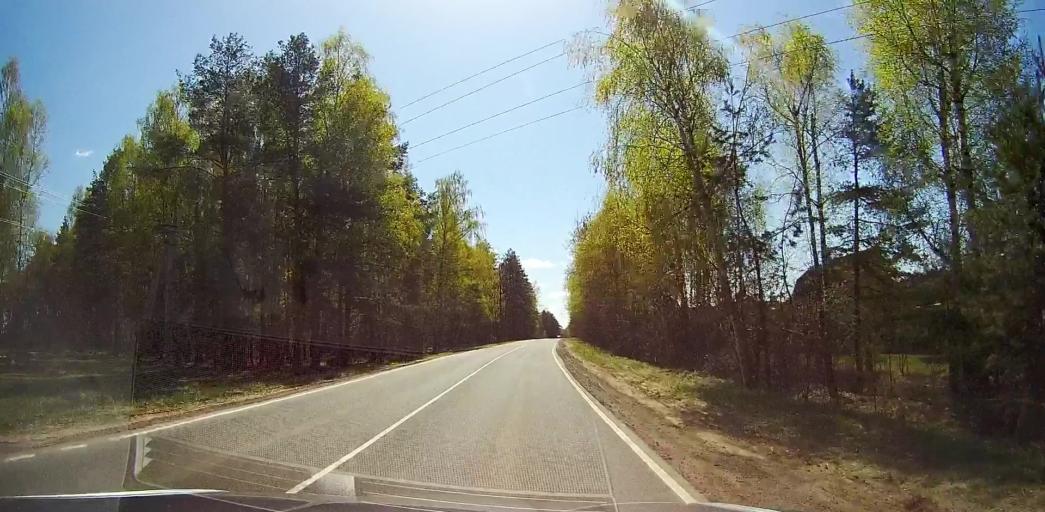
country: RU
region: Moskovskaya
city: Beloozerskiy
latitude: 55.4978
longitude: 38.4307
